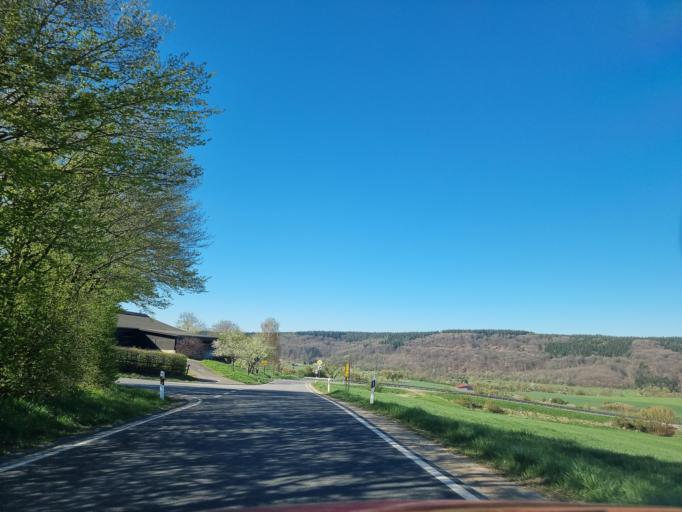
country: DE
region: Rheinland-Pfalz
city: Kaschenbach
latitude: 49.8769
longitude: 6.4796
